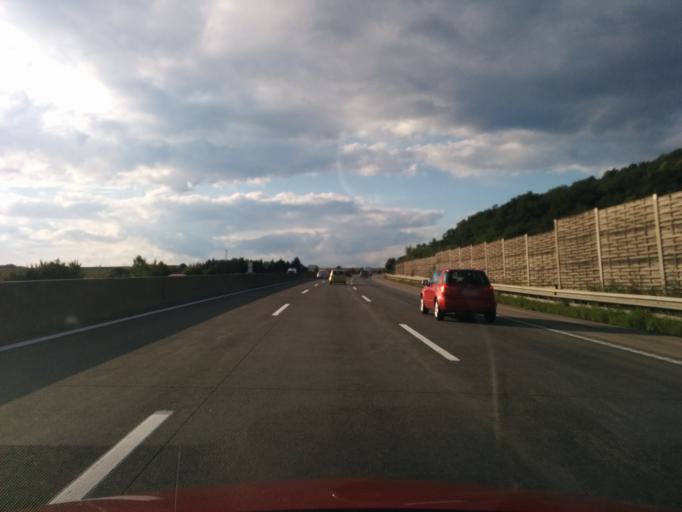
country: AT
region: Lower Austria
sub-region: Politischer Bezirk Melk
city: Loosdorf
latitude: 48.2006
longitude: 15.3681
